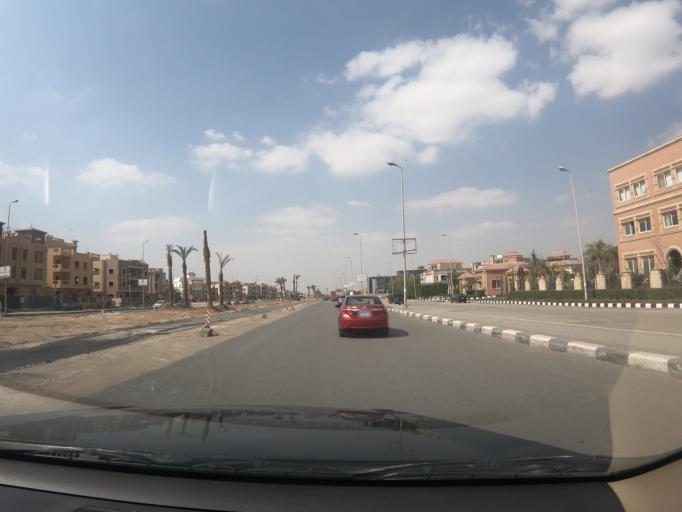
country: EG
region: Muhafazat al Qalyubiyah
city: Al Khankah
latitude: 30.0462
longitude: 31.4751
